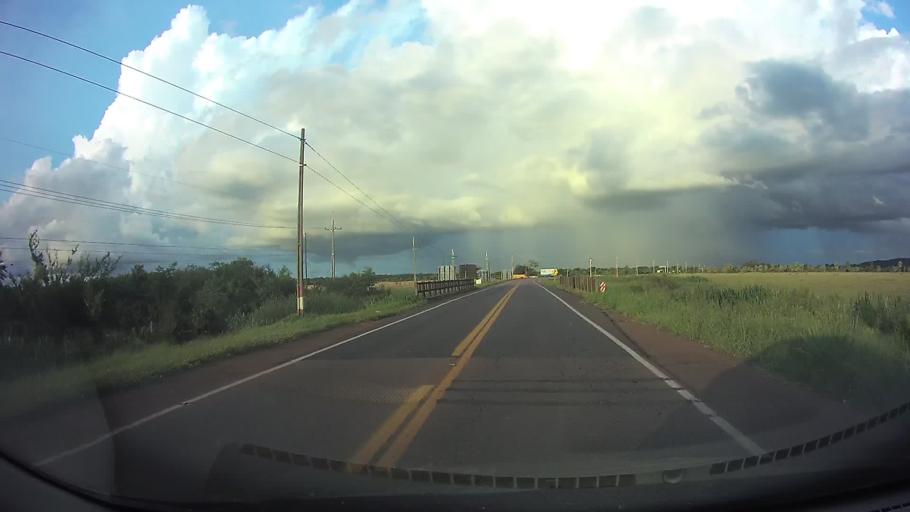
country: PY
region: Paraguari
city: Carapegua
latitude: -25.7549
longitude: -57.2270
